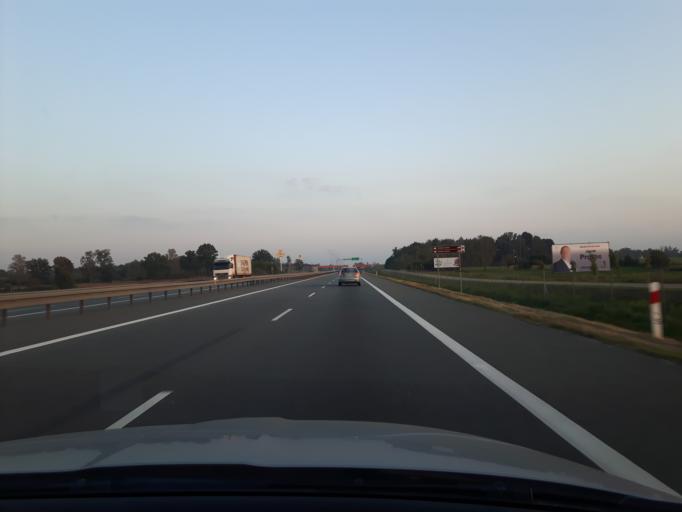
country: PL
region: Warmian-Masurian Voivodeship
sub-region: Powiat elblaski
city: Paslek
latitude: 54.0855
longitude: 19.6015
